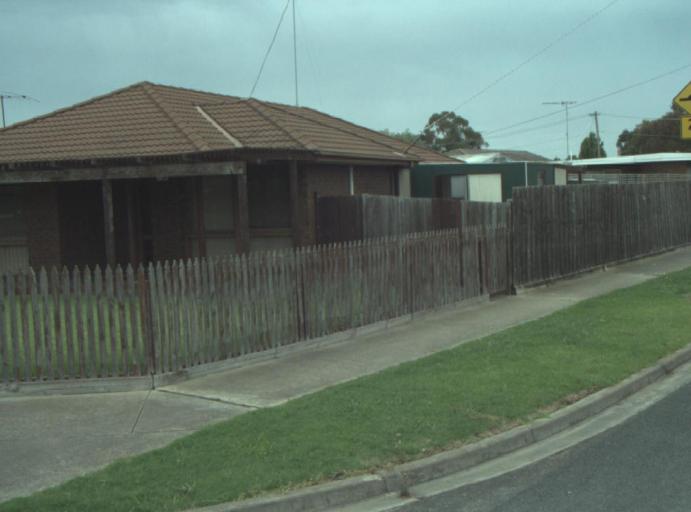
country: AU
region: Victoria
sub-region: Greater Geelong
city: Breakwater
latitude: -38.1761
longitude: 144.3966
